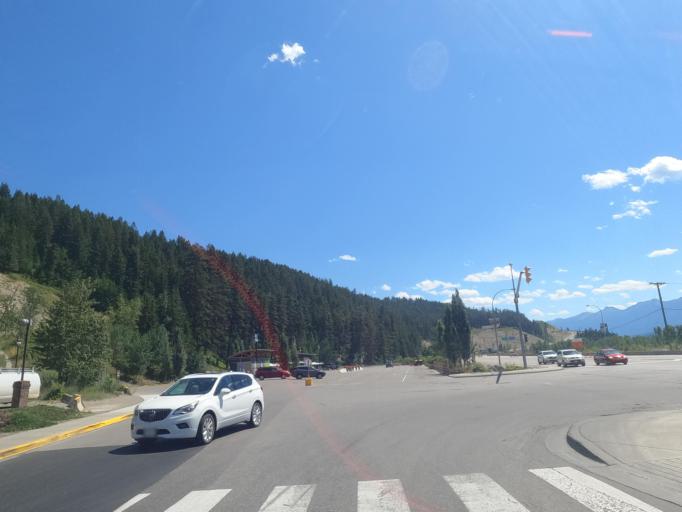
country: CA
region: British Columbia
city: Golden
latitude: 51.3111
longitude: -116.9685
